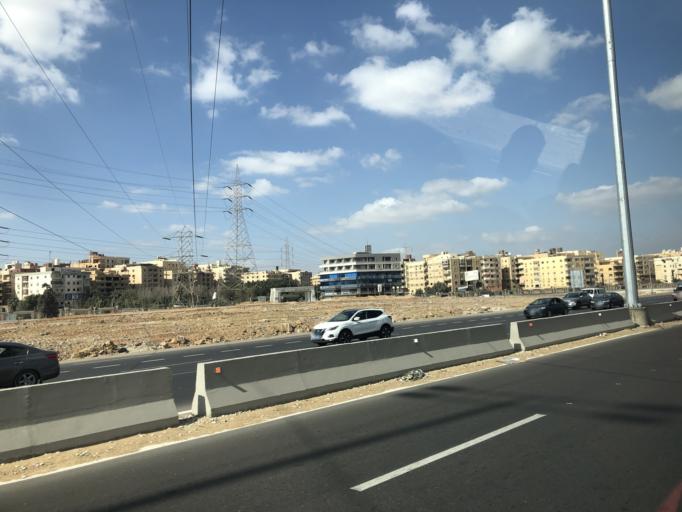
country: EG
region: Al Jizah
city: Al Jizah
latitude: 29.9520
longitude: 31.1049
